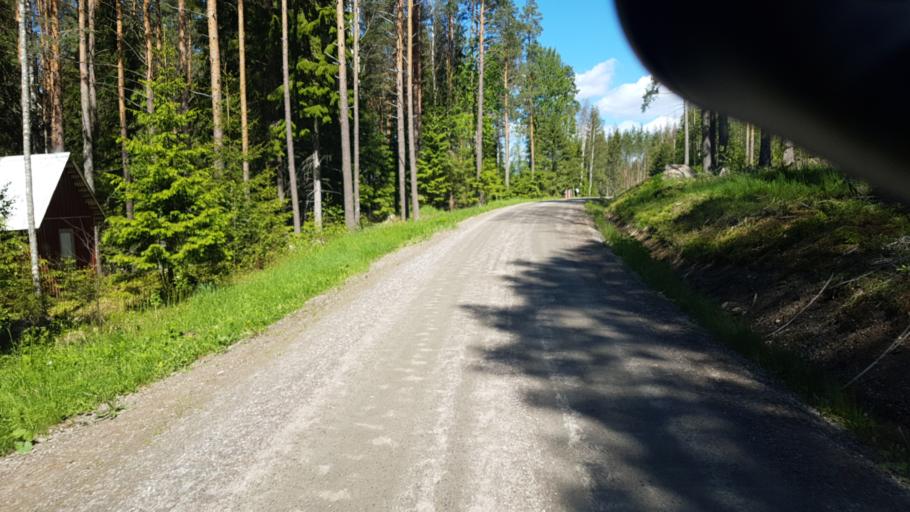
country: SE
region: Vaermland
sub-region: Grums Kommun
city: Grums
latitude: 59.5146
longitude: 12.9279
